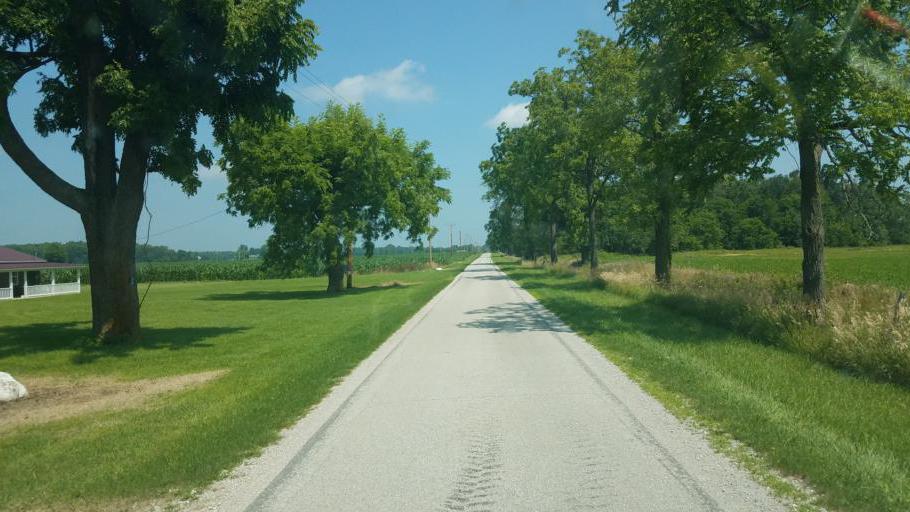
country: US
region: Ohio
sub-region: Seneca County
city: Tiffin
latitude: 41.0272
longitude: -82.9774
